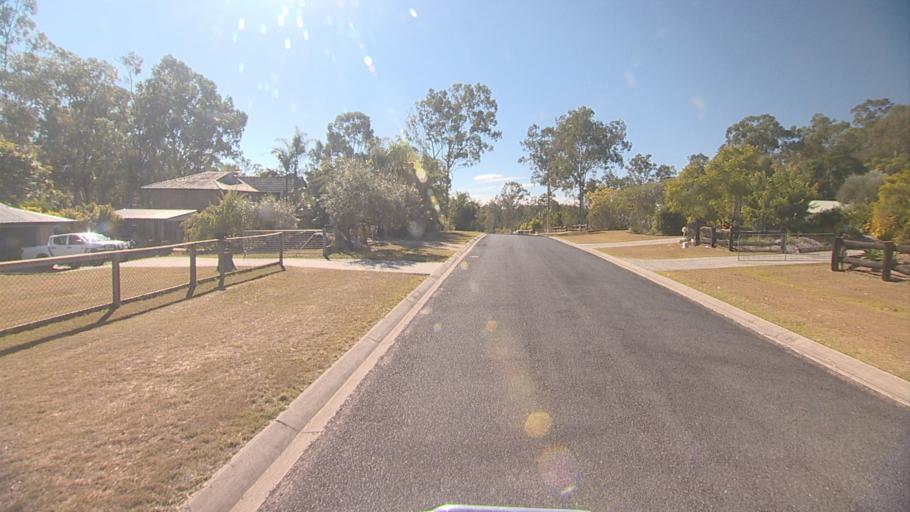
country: AU
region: Queensland
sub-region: Logan
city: North Maclean
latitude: -27.8205
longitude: 152.9448
